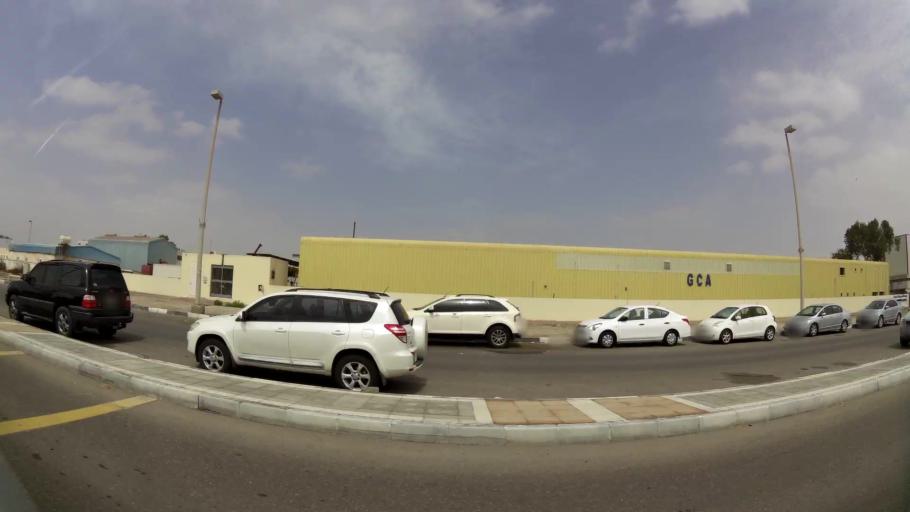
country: AE
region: Abu Dhabi
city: Abu Dhabi
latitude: 24.3813
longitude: 54.4826
